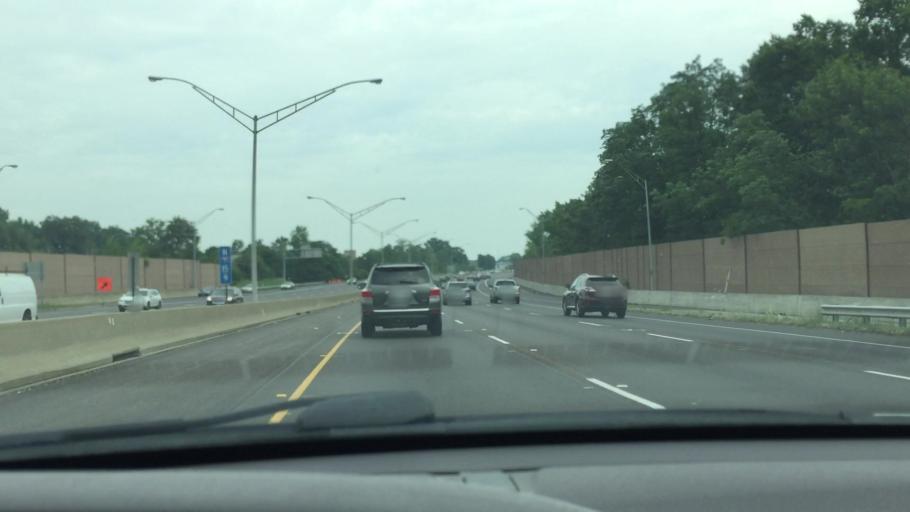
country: US
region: Ohio
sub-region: Hamilton County
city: Blue Ash
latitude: 39.2517
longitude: -84.3647
